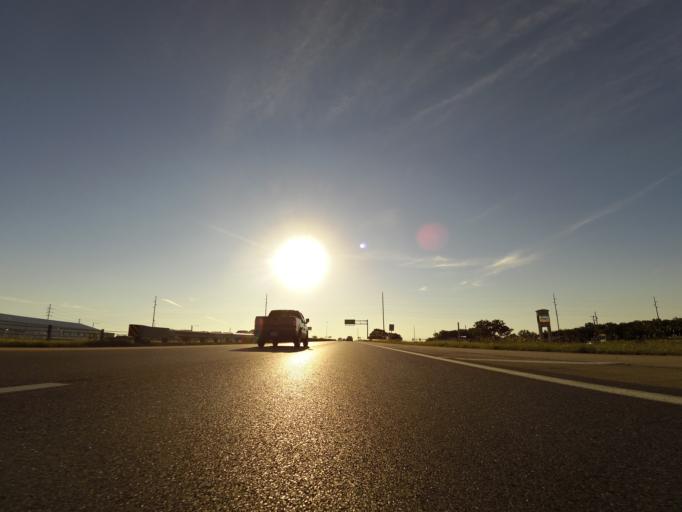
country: US
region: Kansas
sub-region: Sedgwick County
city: Bellaire
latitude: 37.7435
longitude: -97.3010
